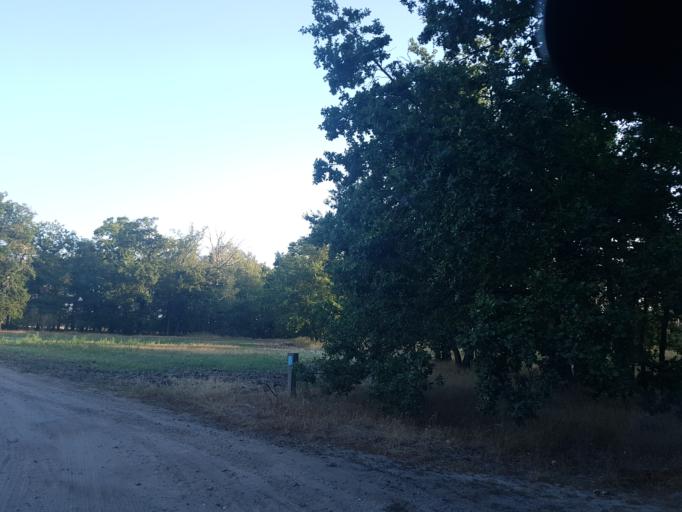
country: DE
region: Brandenburg
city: Herzberg
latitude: 51.6529
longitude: 13.2837
